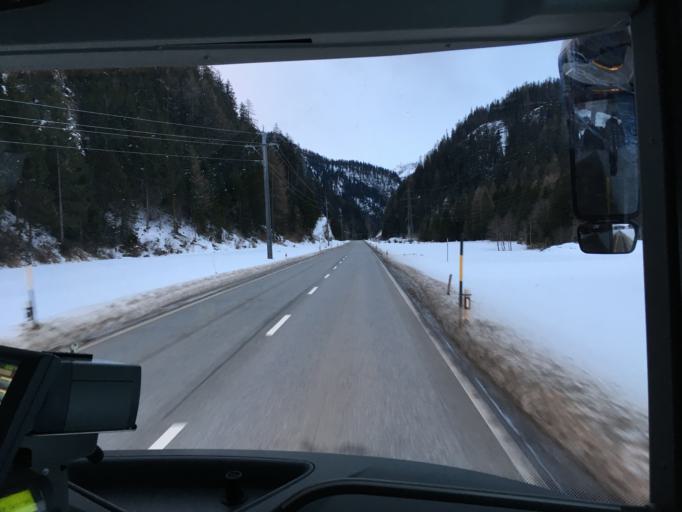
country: CH
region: Grisons
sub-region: Albula District
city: Tiefencastel
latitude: 46.5495
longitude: 9.6251
